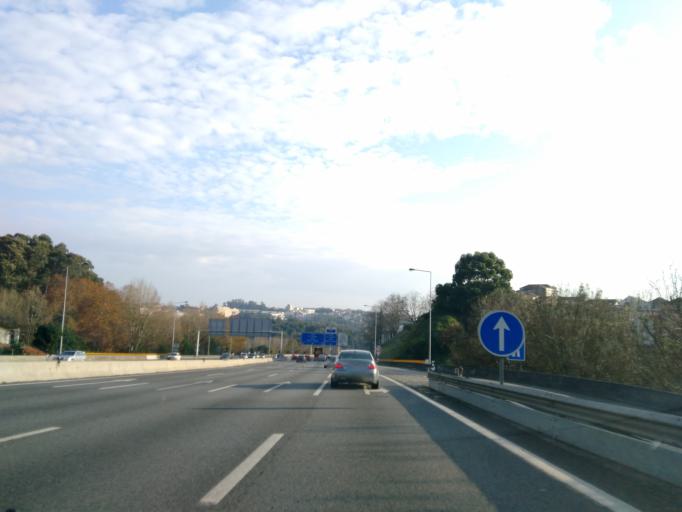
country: PT
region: Porto
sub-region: Gondomar
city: Valbom
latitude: 41.1531
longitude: -8.5817
